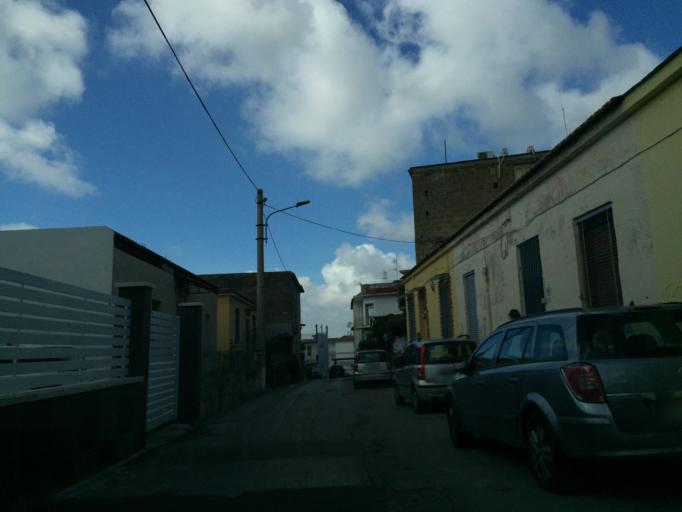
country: IT
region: Campania
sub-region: Provincia di Napoli
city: Massa di Somma
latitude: 40.8450
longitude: 14.3736
